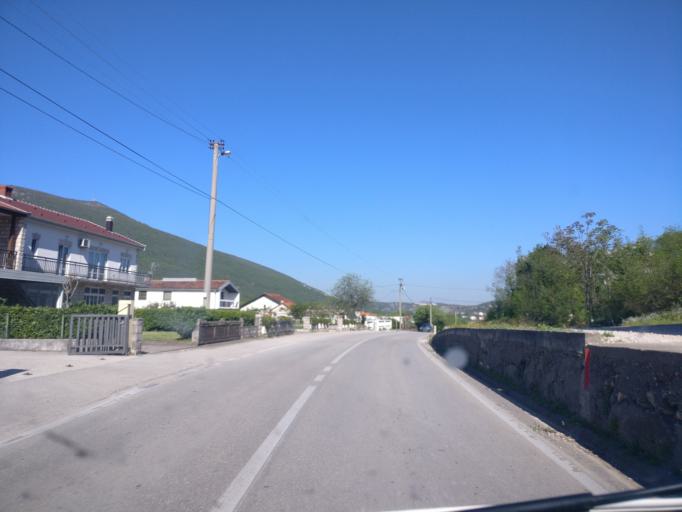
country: BA
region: Federation of Bosnia and Herzegovina
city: Capljina
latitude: 43.1276
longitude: 17.6790
